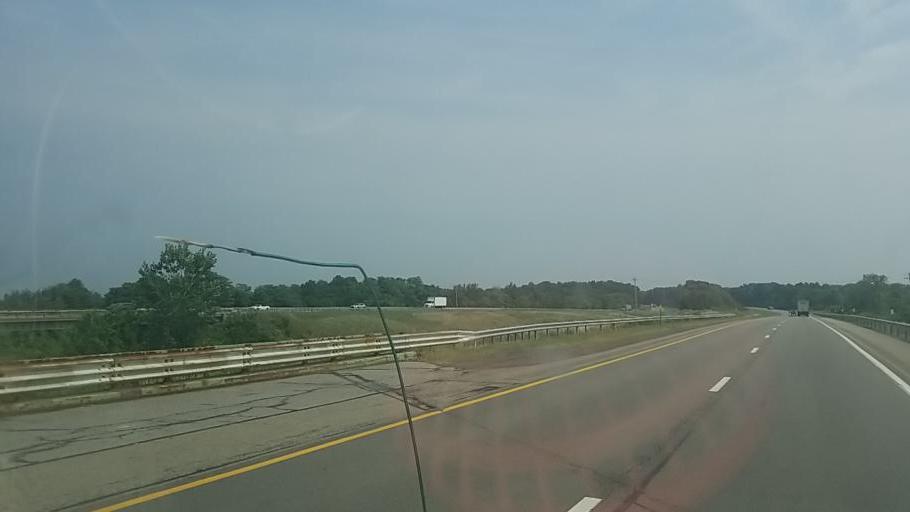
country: US
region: New York
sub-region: Chautauqua County
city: Brocton
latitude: 42.4110
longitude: -79.4247
